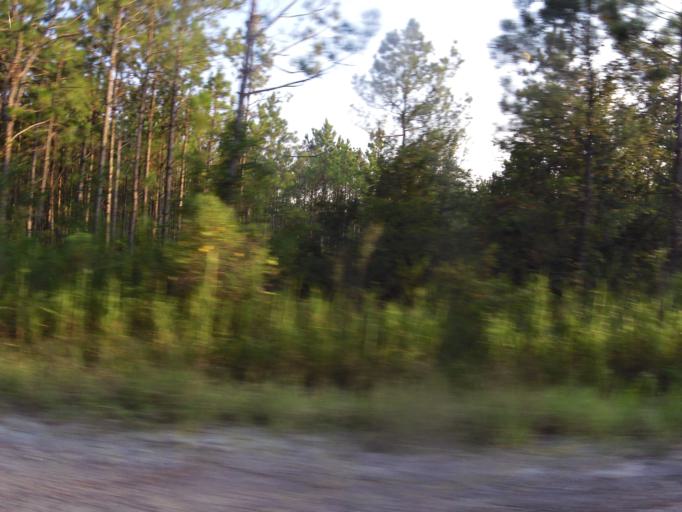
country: US
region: Florida
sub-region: Baker County
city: Macclenny
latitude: 30.3953
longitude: -82.1198
